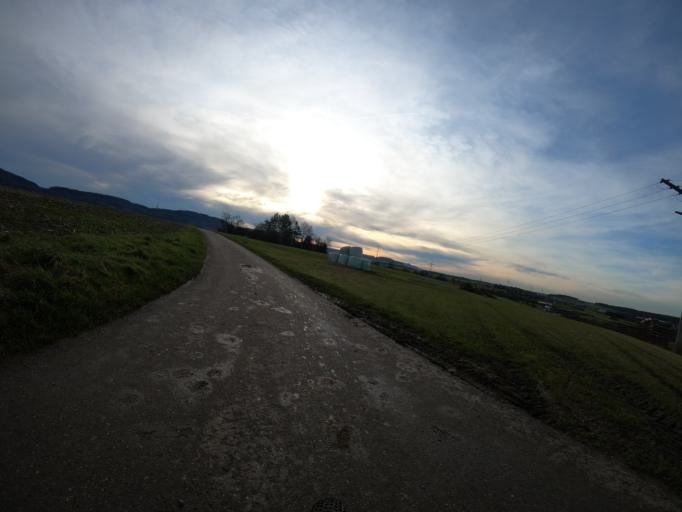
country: DE
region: Baden-Wuerttemberg
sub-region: Regierungsbezirk Stuttgart
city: Heiningen
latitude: 48.6778
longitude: 9.6528
